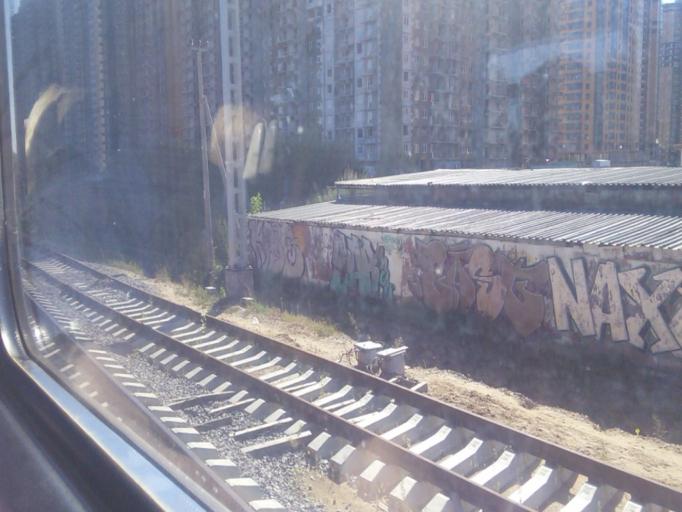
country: RU
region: Moskovskaya
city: Reutov
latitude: 55.7560
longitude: 37.8790
